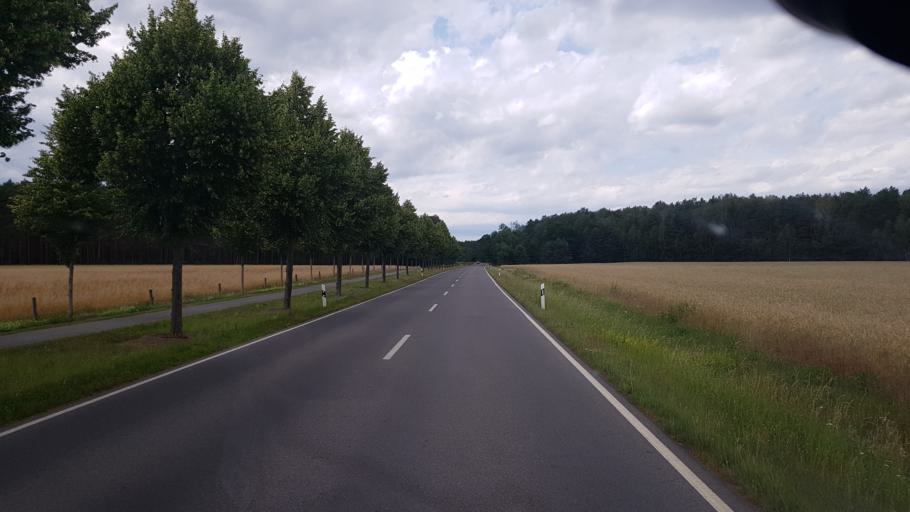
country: DE
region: Brandenburg
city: Sallgast
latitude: 51.6212
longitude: 13.7922
